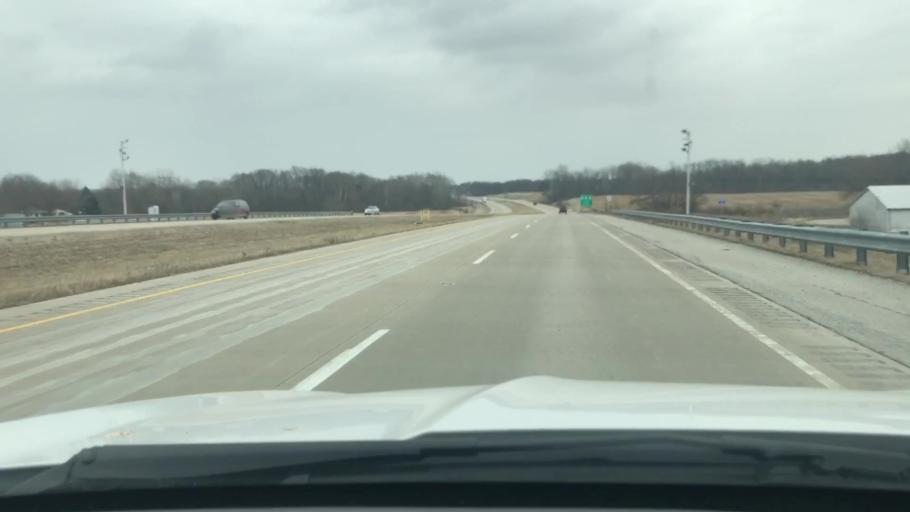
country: US
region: Indiana
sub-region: Cass County
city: Dunkirk
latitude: 40.7277
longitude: -86.4063
